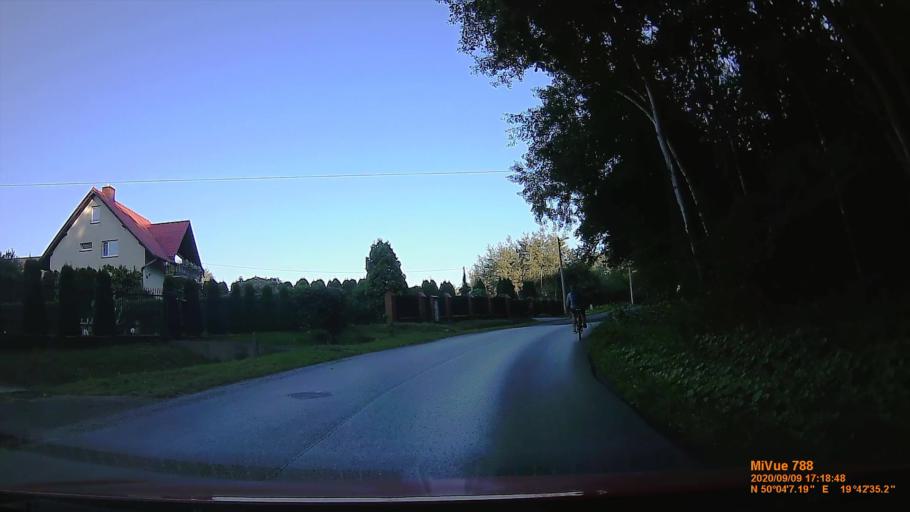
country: PL
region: Lesser Poland Voivodeship
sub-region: Powiat krakowski
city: Czulow
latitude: 50.0687
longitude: 19.7098
